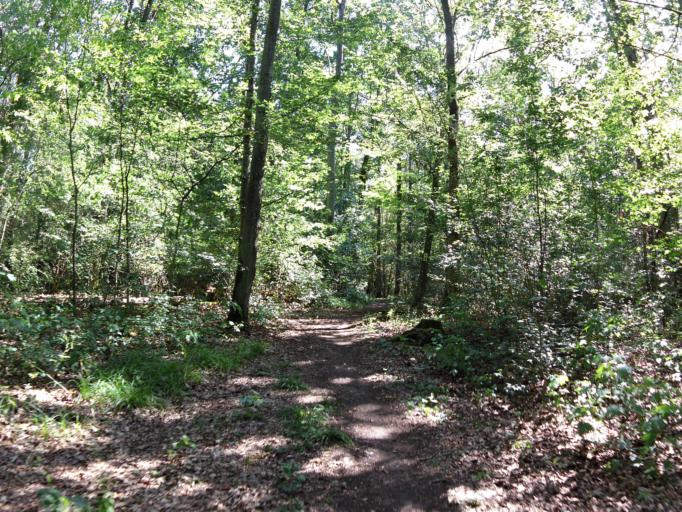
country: DE
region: Bavaria
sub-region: Regierungsbezirk Unterfranken
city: Veitshochheim
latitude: 49.8470
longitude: 9.8890
